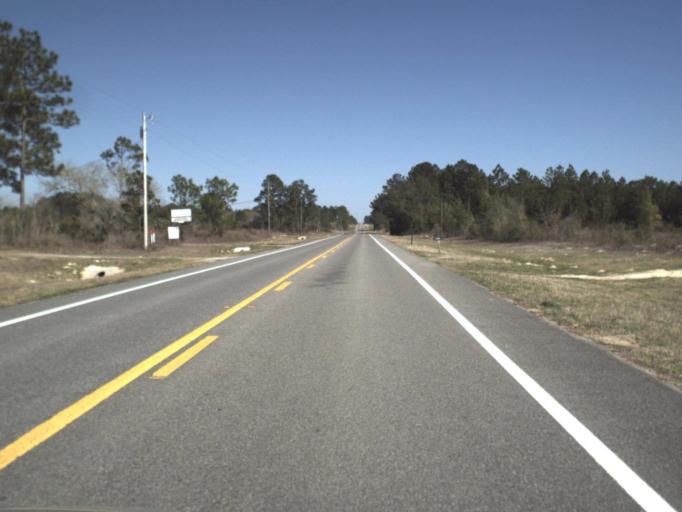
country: US
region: Florida
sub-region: Bay County
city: Youngstown
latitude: 30.4360
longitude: -85.4582
